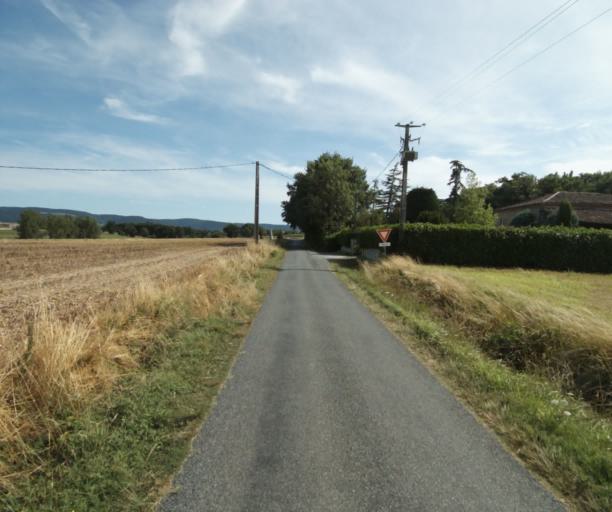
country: FR
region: Midi-Pyrenees
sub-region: Departement du Tarn
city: Soreze
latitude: 43.5014
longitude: 2.0471
